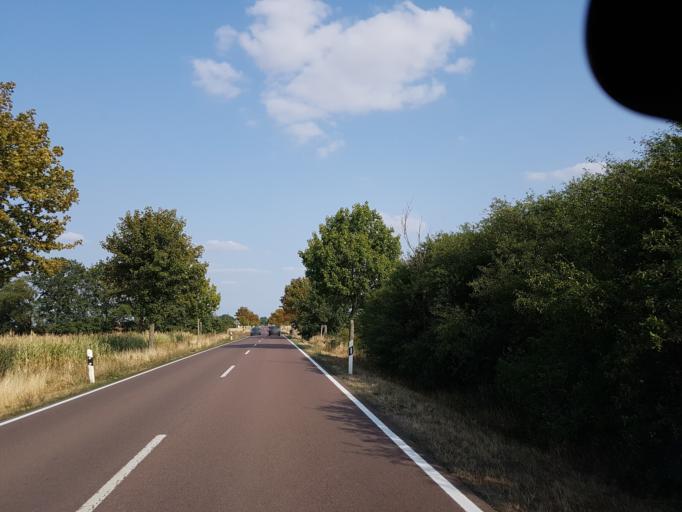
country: DE
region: Saxony-Anhalt
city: Kemberg
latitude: 51.8061
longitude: 12.6619
